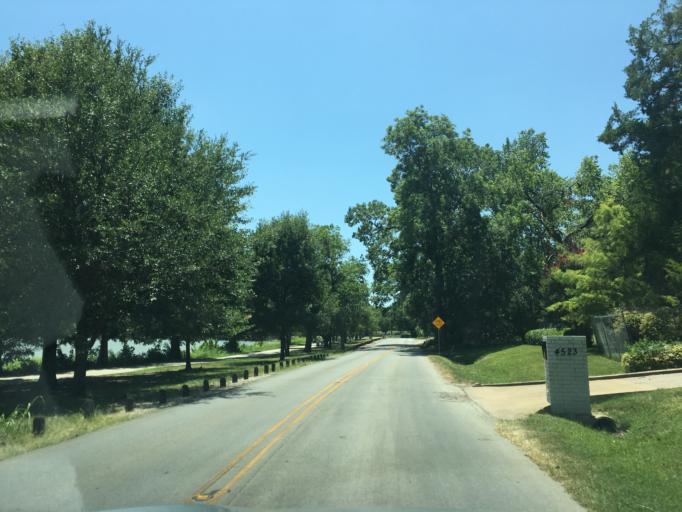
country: US
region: Texas
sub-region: Dallas County
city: Highland Park
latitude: 32.8427
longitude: -96.7301
